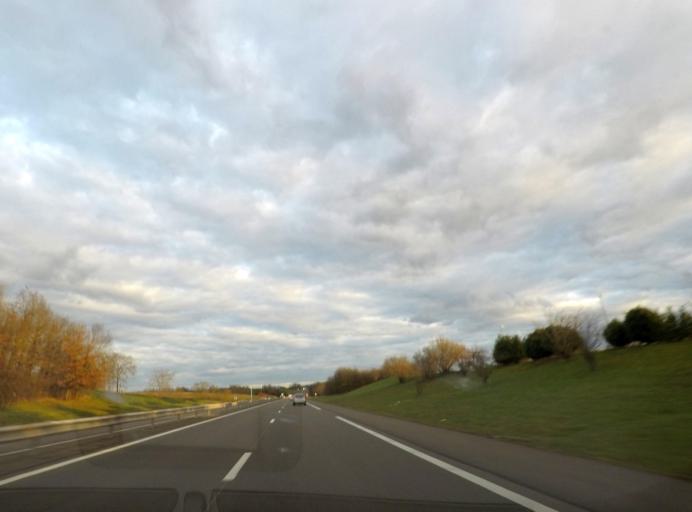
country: FR
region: Rhone-Alpes
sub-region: Departement de l'Ain
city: Saint-Cyr-sur-Menthon
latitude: 46.2788
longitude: 4.9838
